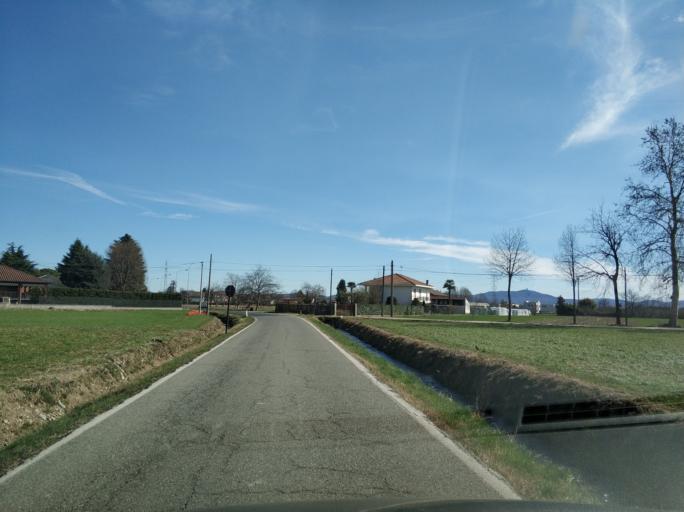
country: IT
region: Piedmont
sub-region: Provincia di Torino
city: Leini
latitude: 45.1892
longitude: 7.7009
